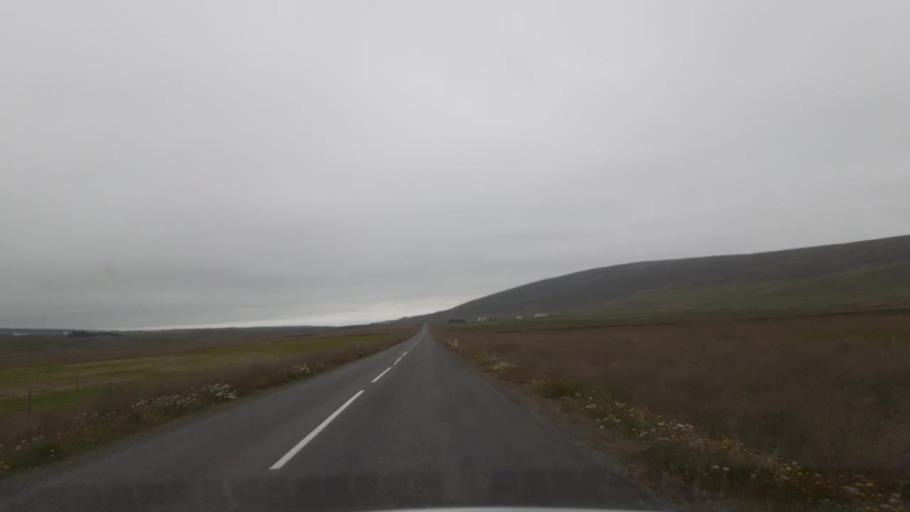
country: IS
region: Northeast
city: Siglufjoerdur
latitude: 65.7421
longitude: -19.1464
